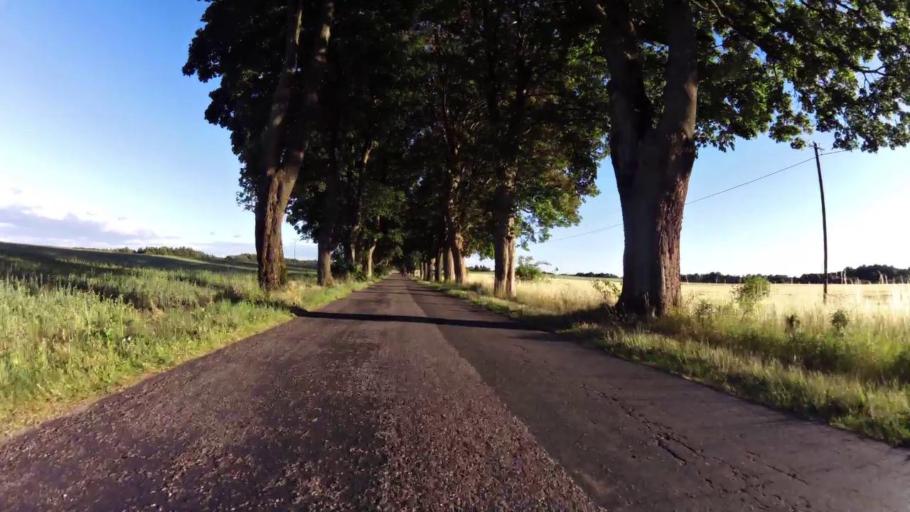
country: PL
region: West Pomeranian Voivodeship
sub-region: Powiat swidwinski
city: Swidwin
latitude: 53.7510
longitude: 15.6899
